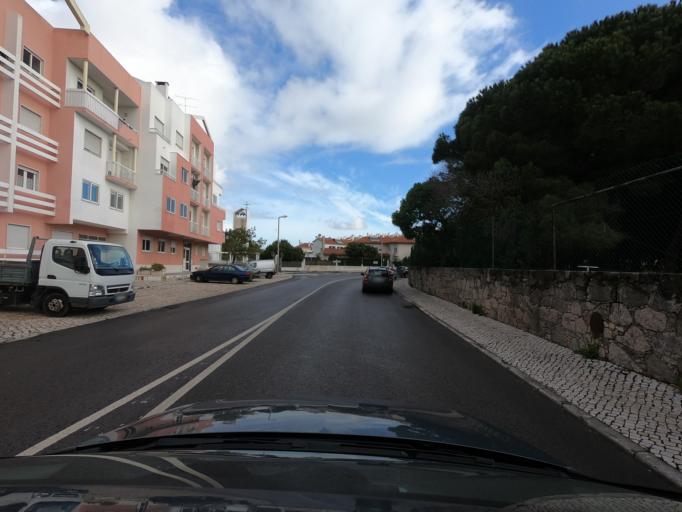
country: PT
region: Lisbon
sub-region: Cascais
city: Sao Domingos de Rana
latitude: 38.7029
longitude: -9.3246
